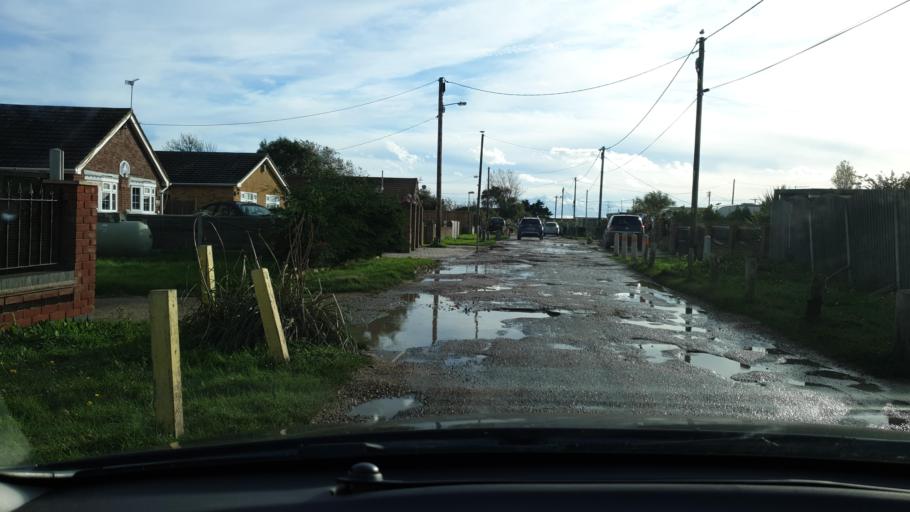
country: GB
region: England
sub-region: Essex
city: Saint Osyth
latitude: 51.7750
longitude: 1.0836
